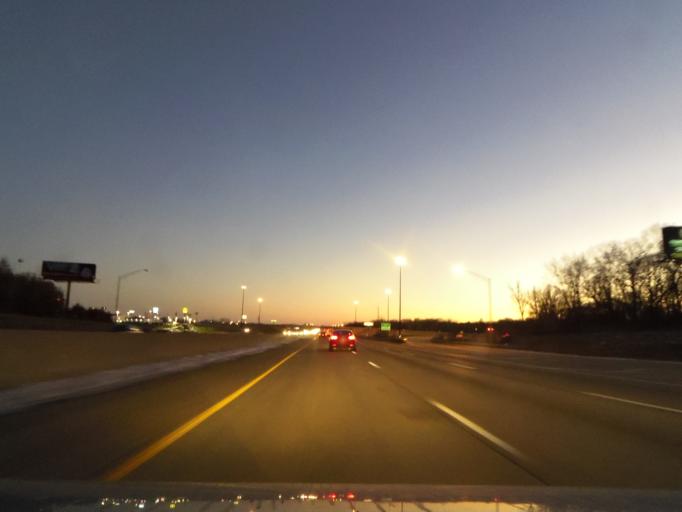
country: US
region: Indiana
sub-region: Lake County
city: Merrillville
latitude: 41.5119
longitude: -87.3200
